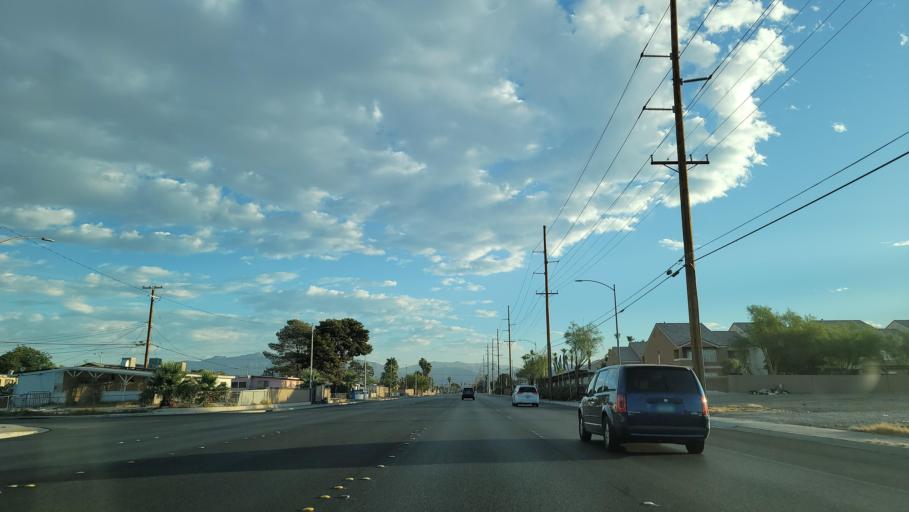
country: US
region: Nevada
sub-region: Clark County
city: North Las Vegas
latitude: 36.1912
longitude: -115.0983
